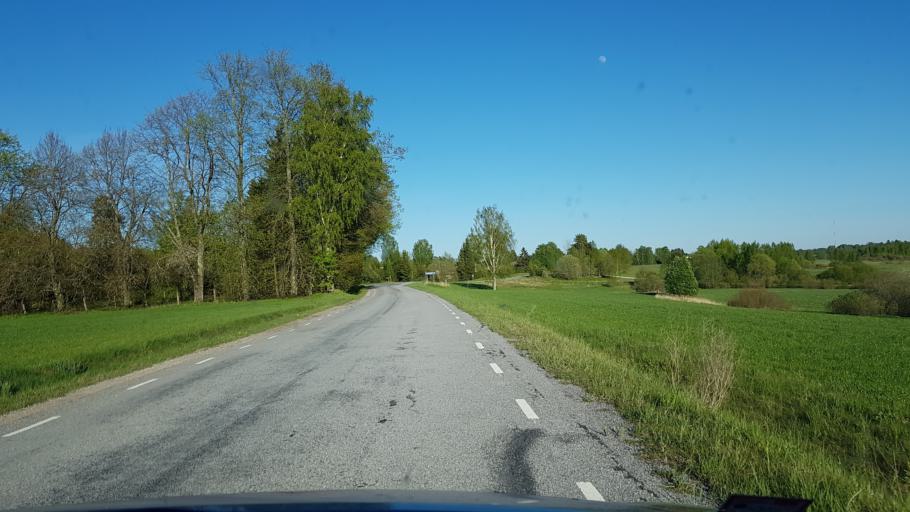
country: EE
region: Vorumaa
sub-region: Voru linn
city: Voru
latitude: 57.9082
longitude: 26.9726
